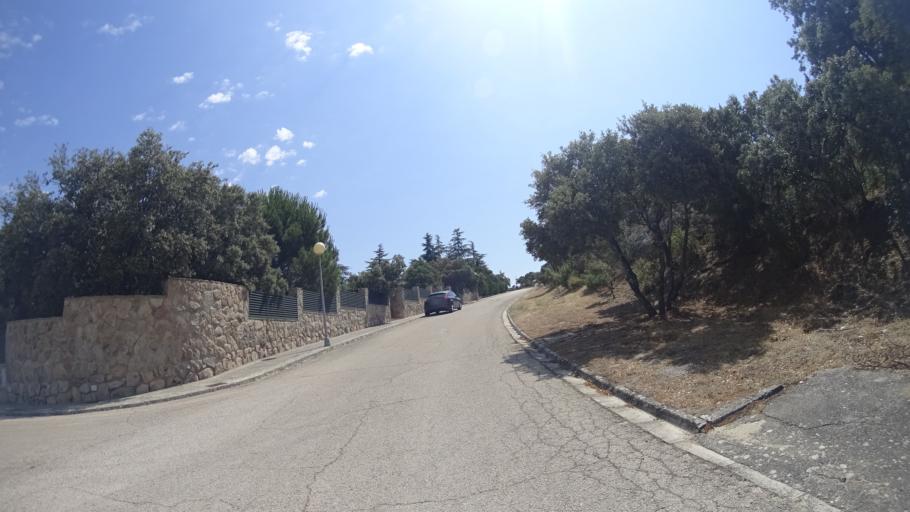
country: ES
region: Madrid
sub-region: Provincia de Madrid
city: Torrelodones
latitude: 40.5995
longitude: -3.9335
